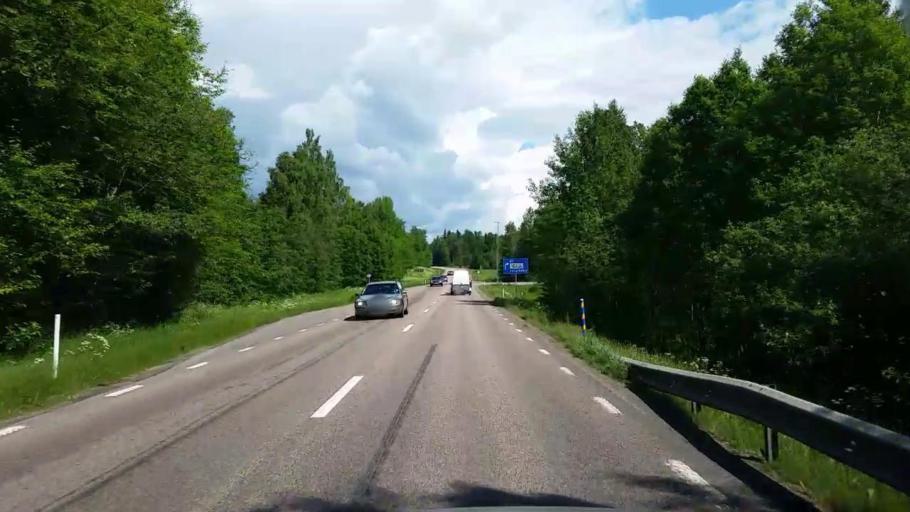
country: SE
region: Dalarna
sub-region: Avesta Kommun
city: Avesta
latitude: 60.1649
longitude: 16.2732
